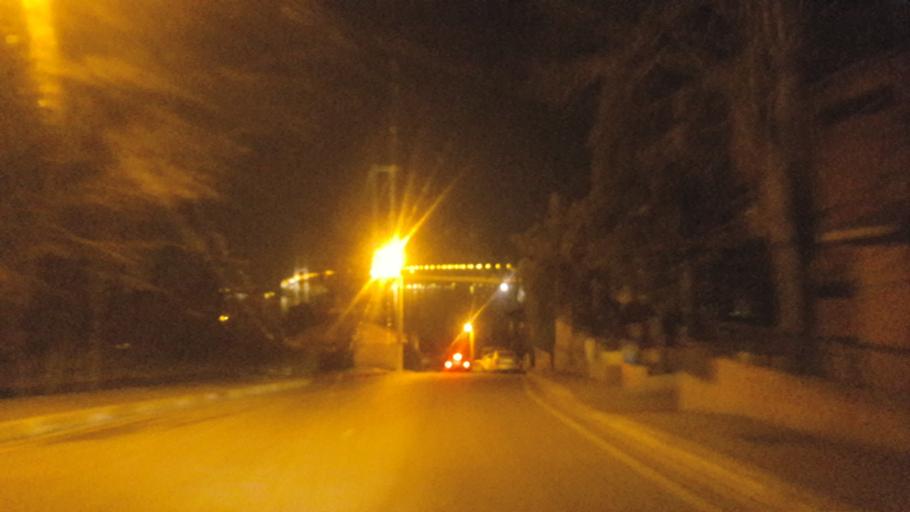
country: TR
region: Kocaeli
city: Tavsanli
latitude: 40.7709
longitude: 29.5211
